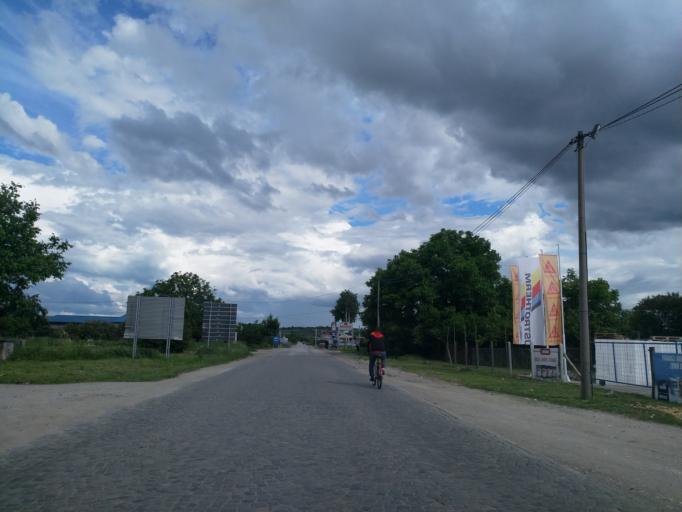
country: RS
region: Central Serbia
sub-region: Pomoravski Okrug
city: Jagodina
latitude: 43.9623
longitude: 21.2807
